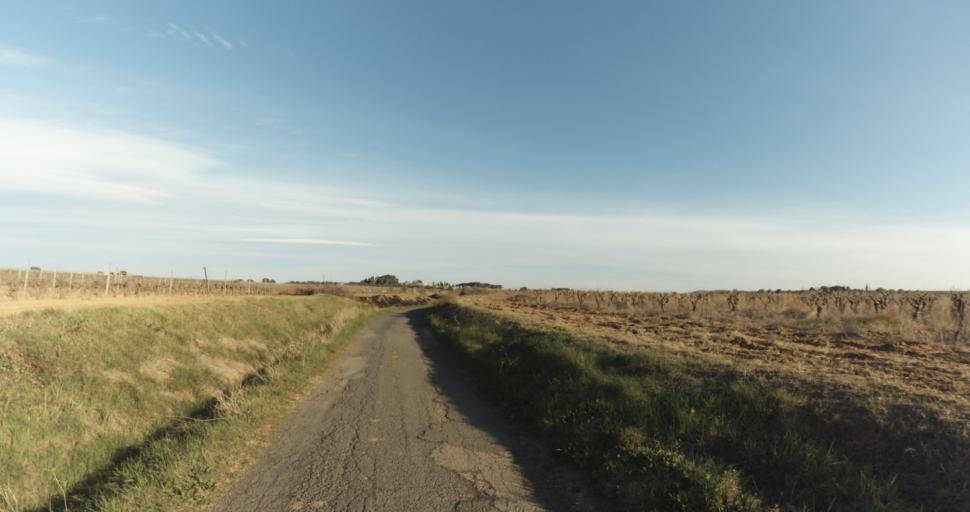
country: FR
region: Languedoc-Roussillon
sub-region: Departement de l'Herault
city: Marseillan
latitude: 43.3748
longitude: 3.5248
